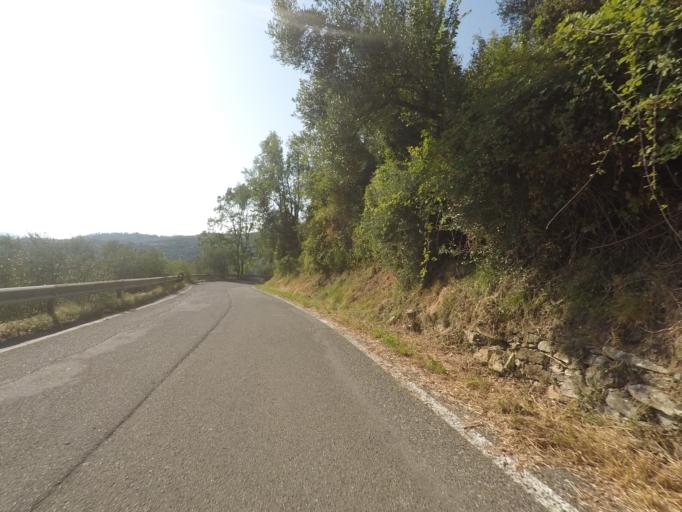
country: IT
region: Liguria
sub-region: Provincia di La Spezia
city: Casano-Dogana-Isola
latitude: 44.0886
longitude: 10.0500
